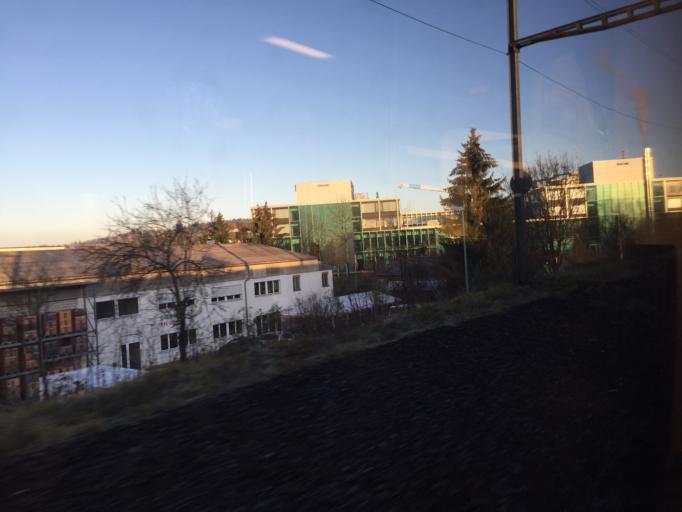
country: CH
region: Zug
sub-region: Zug
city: Baar
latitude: 47.1923
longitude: 8.5183
